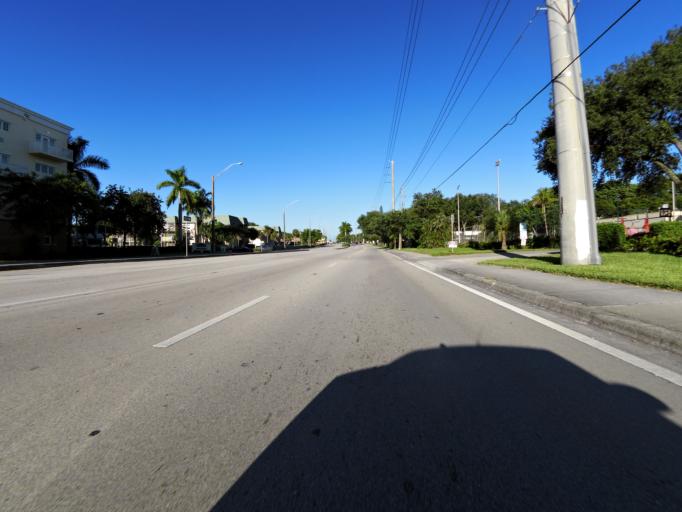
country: US
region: Florida
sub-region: Broward County
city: Davie
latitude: 26.0470
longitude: -80.2030
